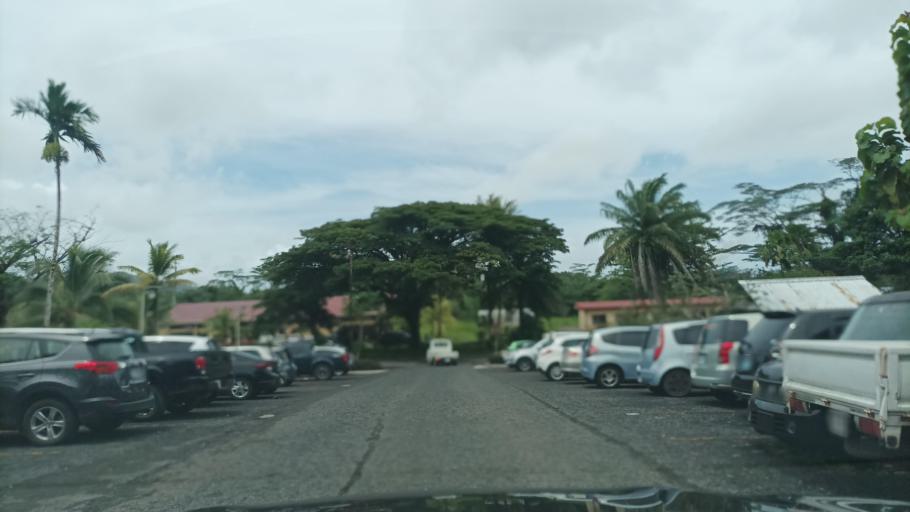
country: FM
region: Pohnpei
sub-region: Sokehs Municipality
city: Palikir - National Government Center
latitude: 6.9240
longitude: 158.1585
